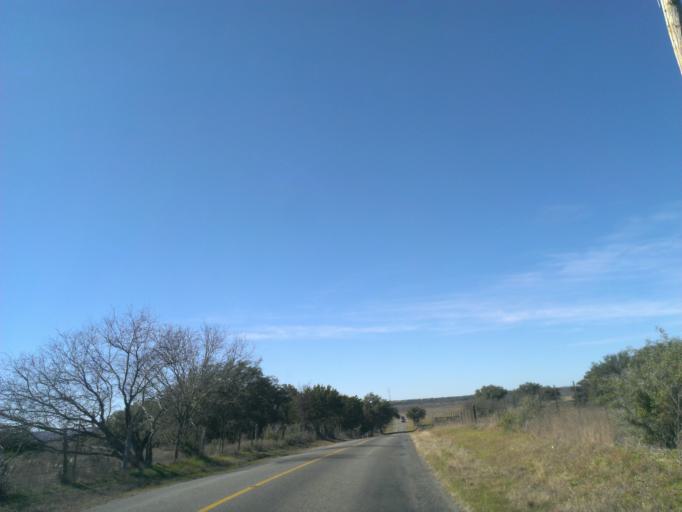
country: US
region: Texas
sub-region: Travis County
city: Briarcliff
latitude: 30.4757
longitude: -98.1705
